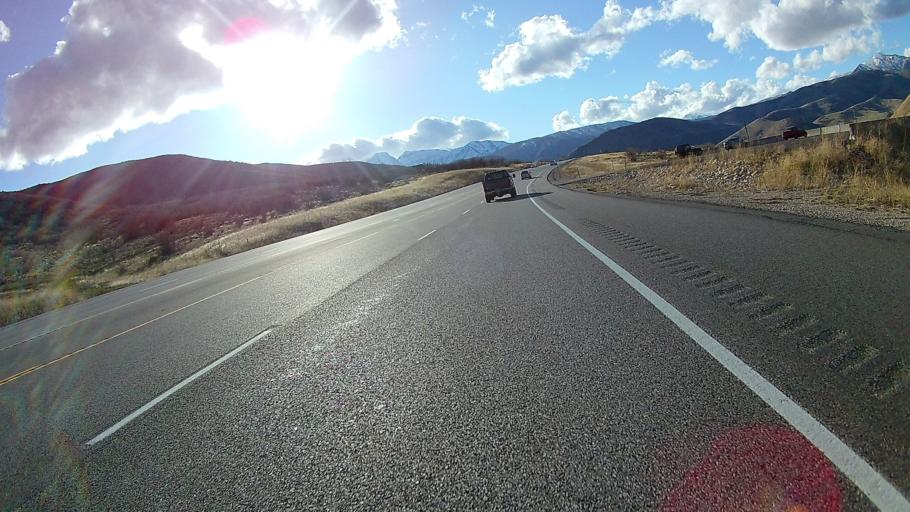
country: US
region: Utah
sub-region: Wasatch County
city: Midway
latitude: 40.4067
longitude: -111.4918
